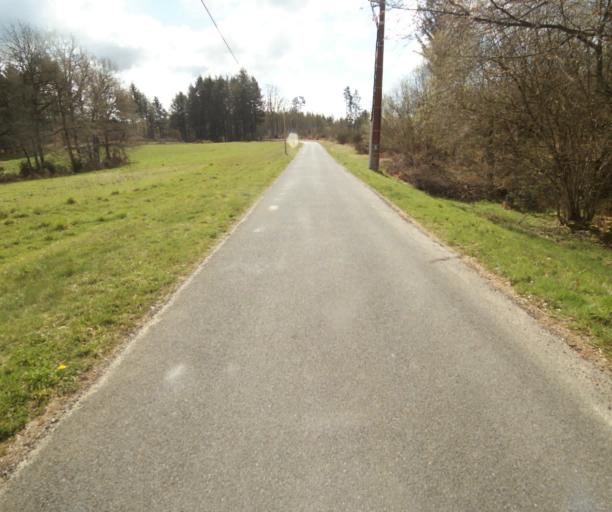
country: FR
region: Limousin
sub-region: Departement de la Correze
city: Argentat
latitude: 45.2434
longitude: 1.9534
